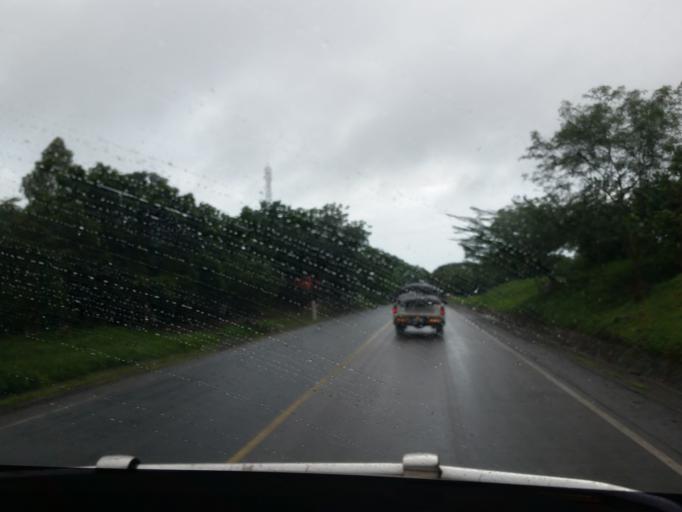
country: NI
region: Matagalpa
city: Terrabona
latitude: 12.5854
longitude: -86.0437
